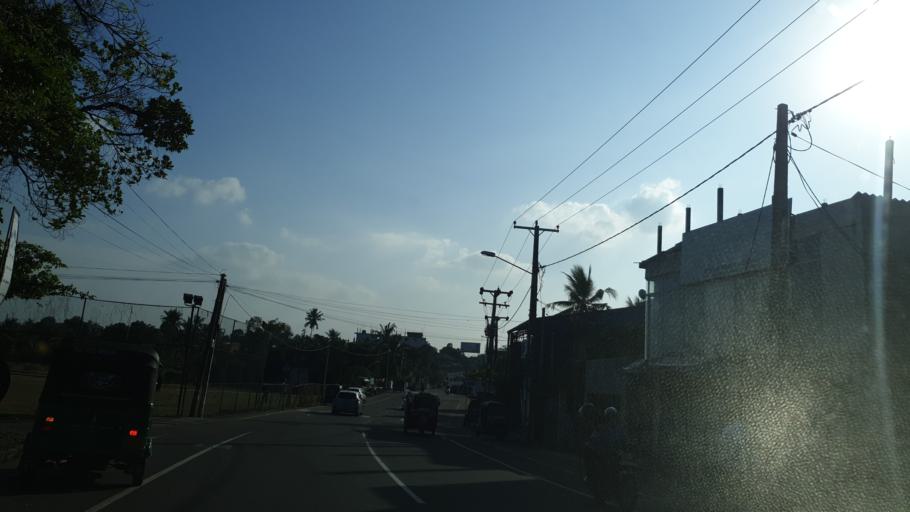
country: LK
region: Western
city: Sri Jayewardenepura Kotte
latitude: 6.8599
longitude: 79.8947
